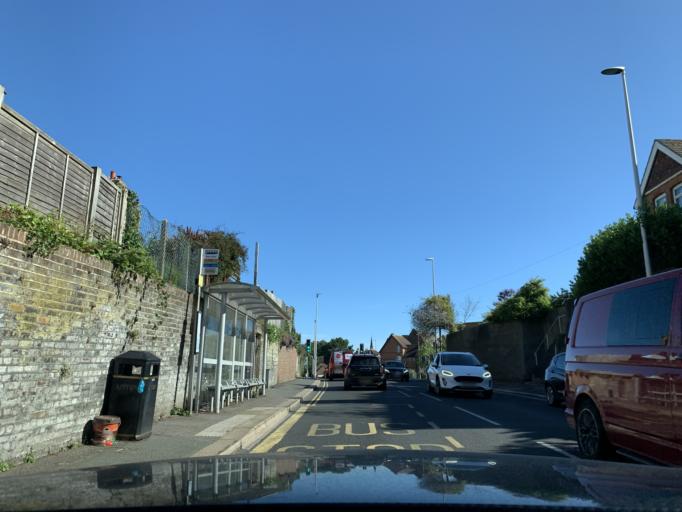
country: GB
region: England
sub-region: East Sussex
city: Saint Leonards-on-Sea
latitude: 50.8690
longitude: 0.5552
